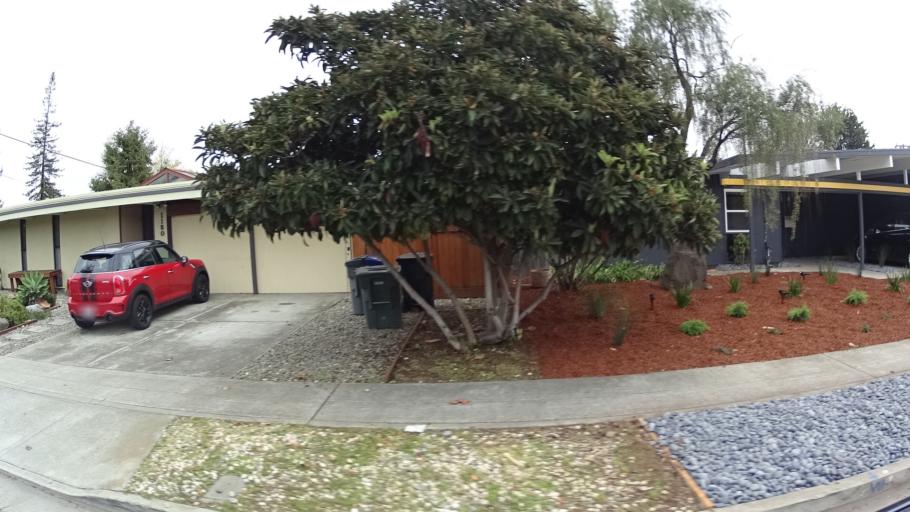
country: US
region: California
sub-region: Santa Clara County
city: Sunnyvale
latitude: 37.3552
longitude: -122.0415
